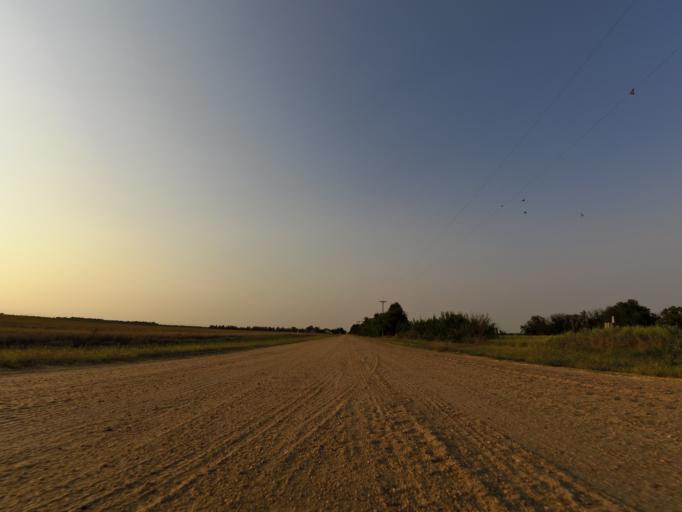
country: US
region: Kansas
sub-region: Reno County
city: South Hutchinson
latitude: 37.9993
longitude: -97.9955
